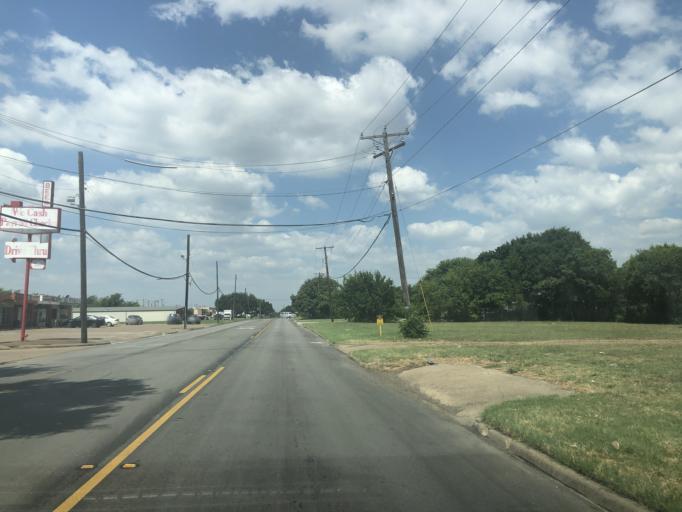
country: US
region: Texas
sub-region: Dallas County
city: Grand Prairie
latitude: 32.7447
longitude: -97.0386
